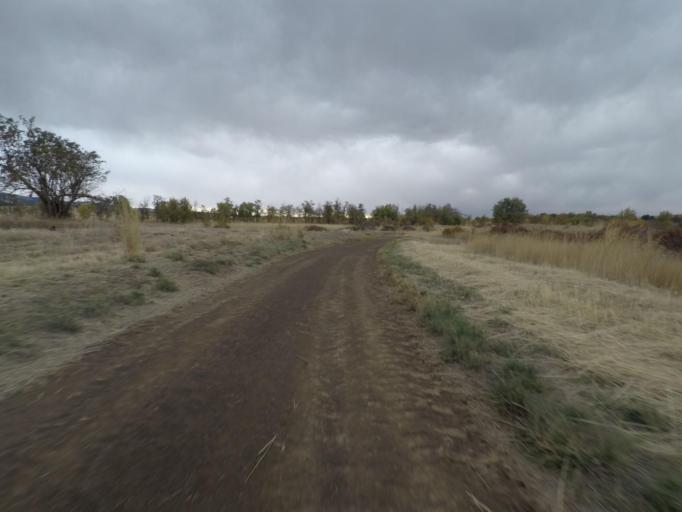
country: US
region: Washington
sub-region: Walla Walla County
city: Walla Walla East
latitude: 46.0747
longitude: -118.2570
